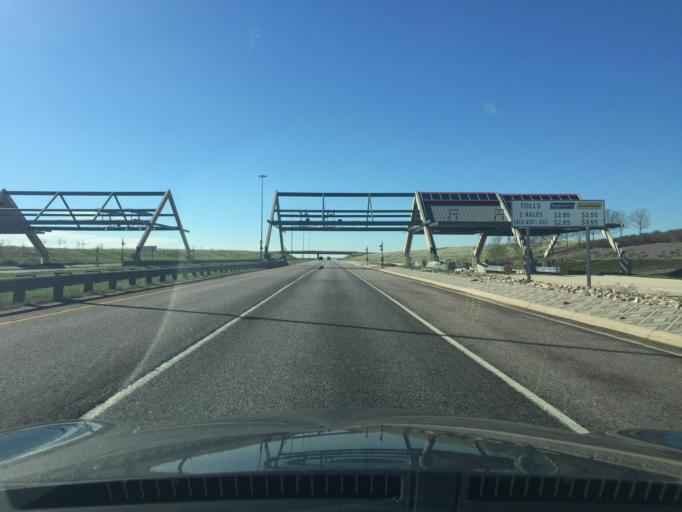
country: US
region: Colorado
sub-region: Adams County
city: Brighton
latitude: 39.8619
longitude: -104.7506
